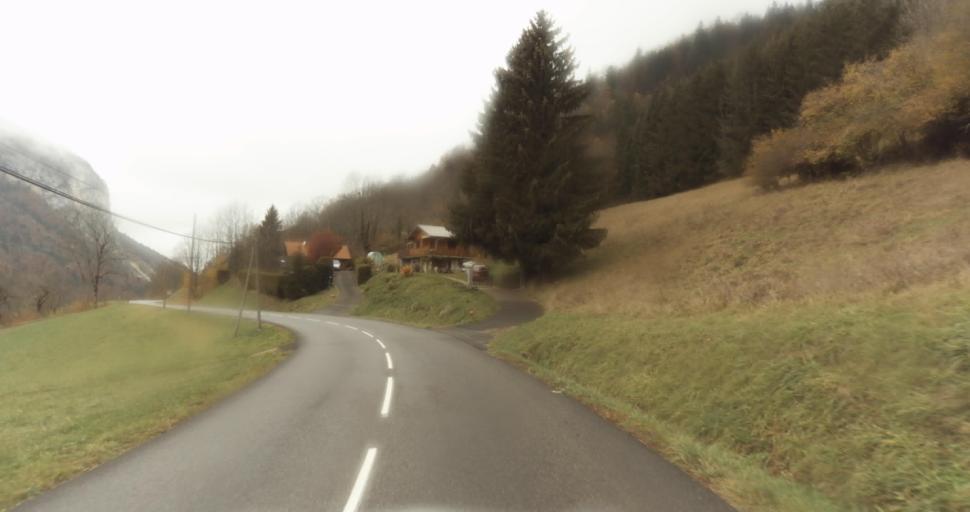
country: FR
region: Rhone-Alpes
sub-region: Departement de la Haute-Savoie
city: Thorens-Glieres
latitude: 45.9858
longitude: 6.2783
